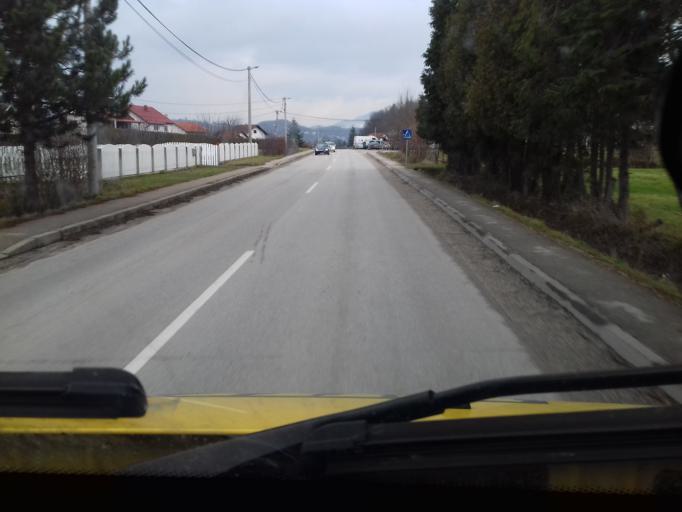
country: BA
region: Federation of Bosnia and Herzegovina
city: Zepce
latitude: 44.4211
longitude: 18.0791
